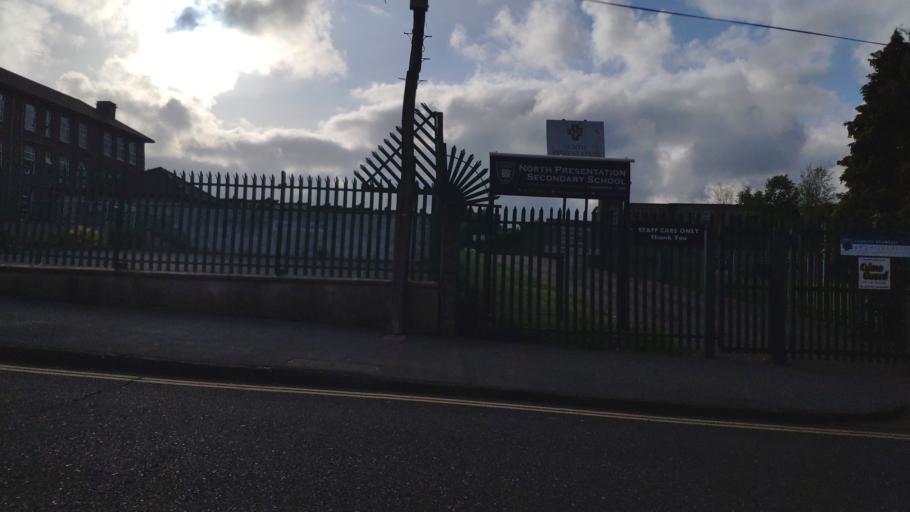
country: IE
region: Munster
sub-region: County Cork
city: Cork
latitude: 51.9111
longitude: -8.4839
